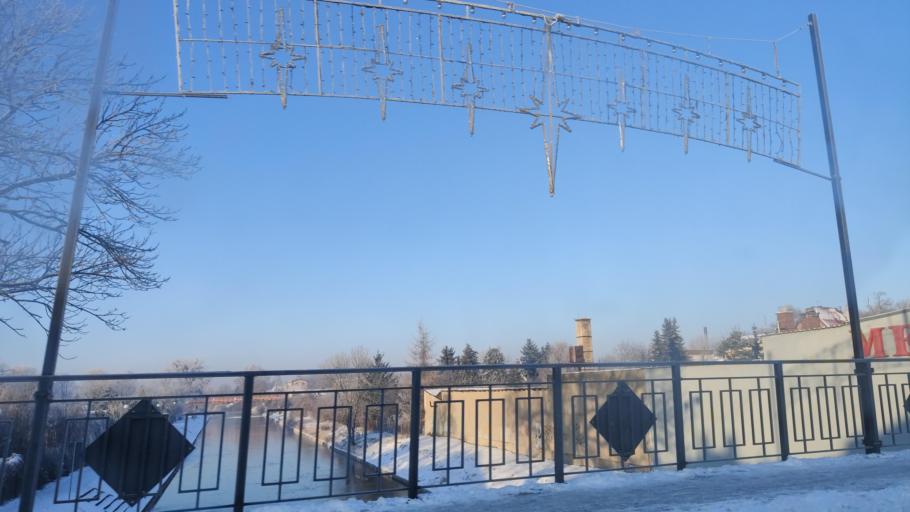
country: PL
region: Kujawsko-Pomorskie
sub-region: Powiat zninski
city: Barcin
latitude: 52.8648
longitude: 17.9458
